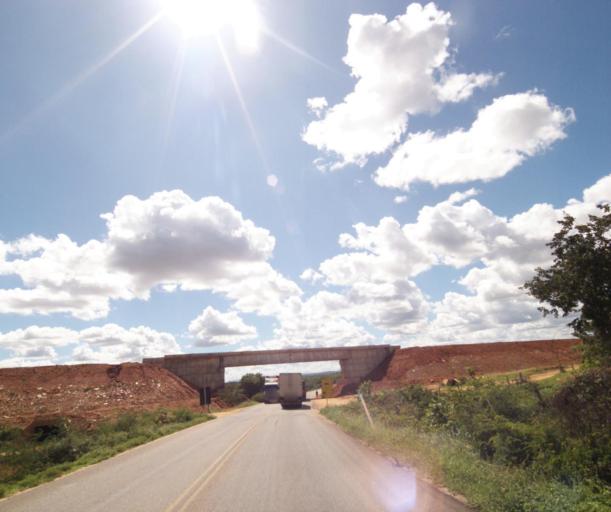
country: BR
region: Bahia
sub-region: Caetite
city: Caetite
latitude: -14.1719
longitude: -42.2201
